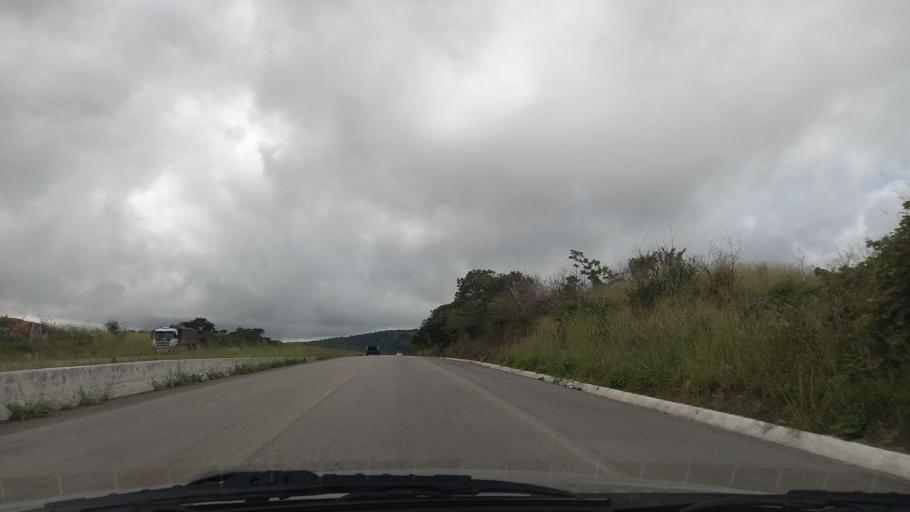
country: BR
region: Pernambuco
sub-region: Caruaru
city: Caruaru
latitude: -8.3254
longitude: -35.9869
